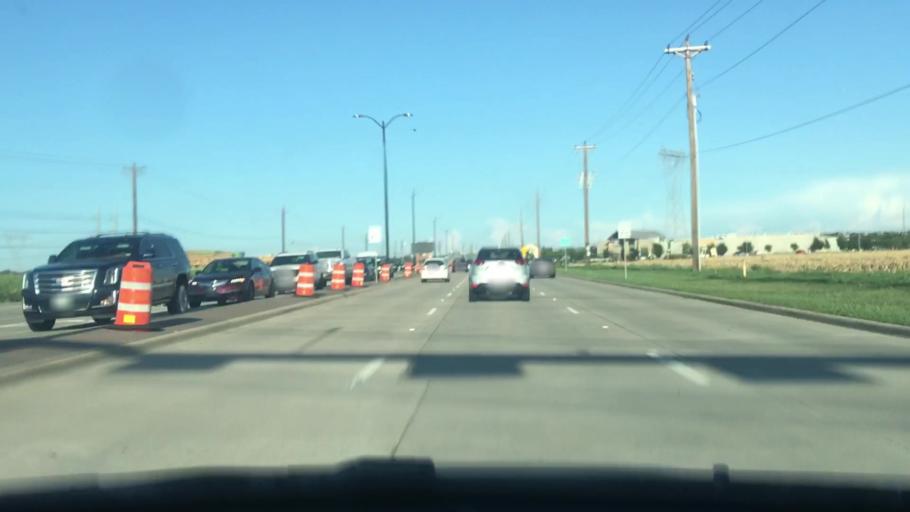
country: US
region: Texas
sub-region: Collin County
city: Frisco
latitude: 33.1749
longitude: -96.8319
